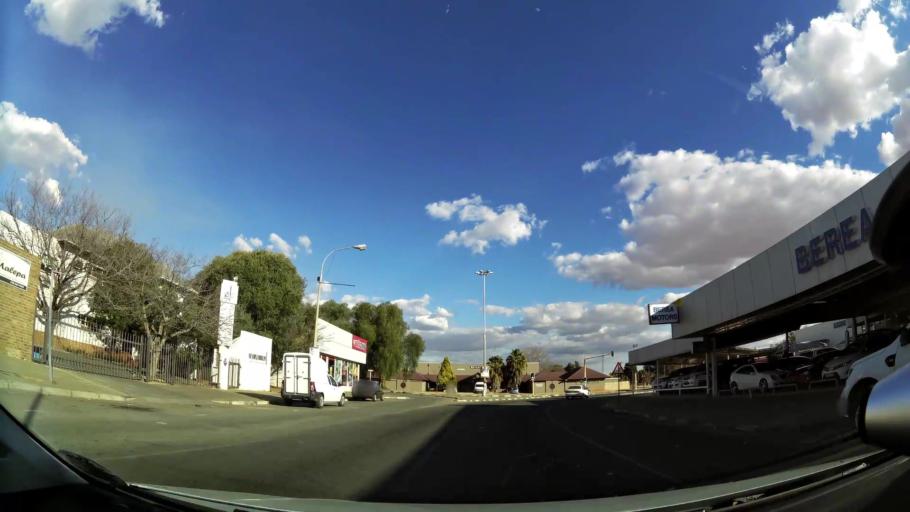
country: ZA
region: North-West
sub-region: Dr Kenneth Kaunda District Municipality
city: Klerksdorp
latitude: -26.8726
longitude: 26.6656
